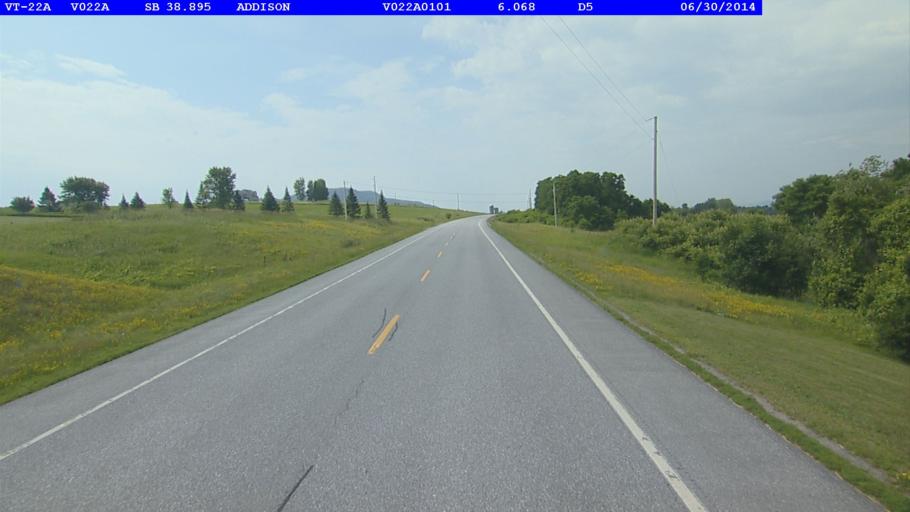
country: US
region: Vermont
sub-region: Addison County
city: Vergennes
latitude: 44.1160
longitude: -73.2937
